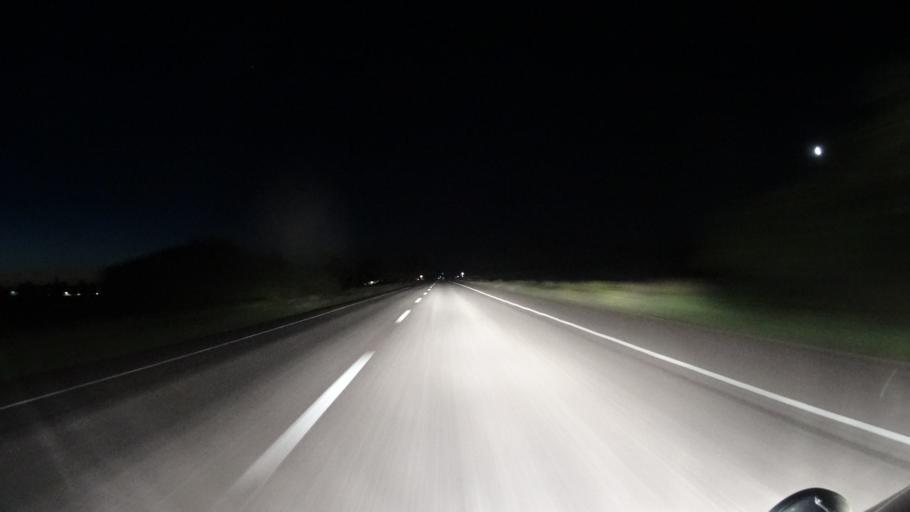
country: SE
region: OEstergoetland
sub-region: Vadstena Kommun
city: Herrestad
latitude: 58.2867
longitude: 14.7711
